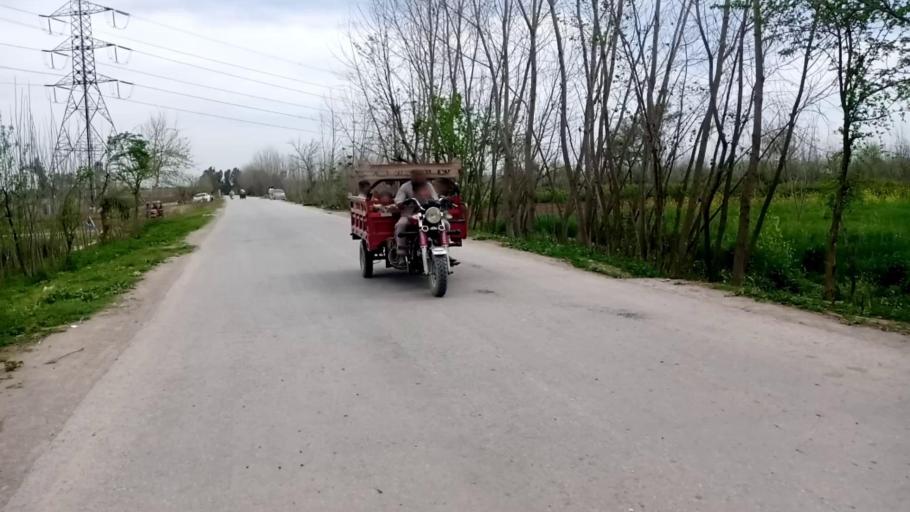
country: PK
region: Khyber Pakhtunkhwa
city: Charsadda
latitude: 34.0626
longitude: 71.6948
